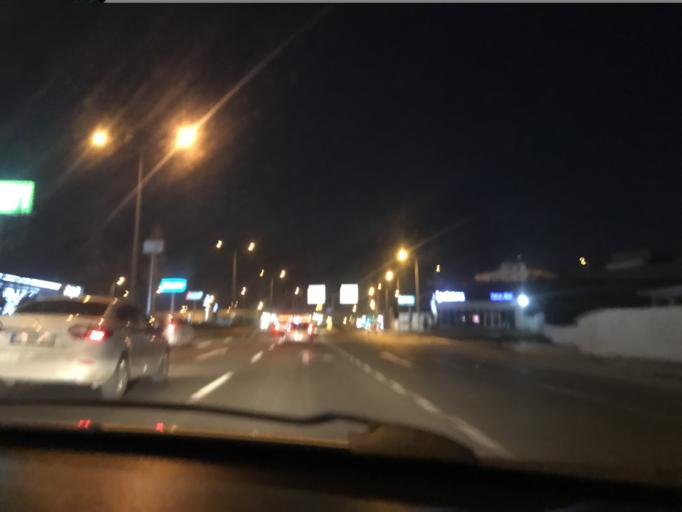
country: TR
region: Ankara
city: Batikent
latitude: 39.9454
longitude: 32.7161
